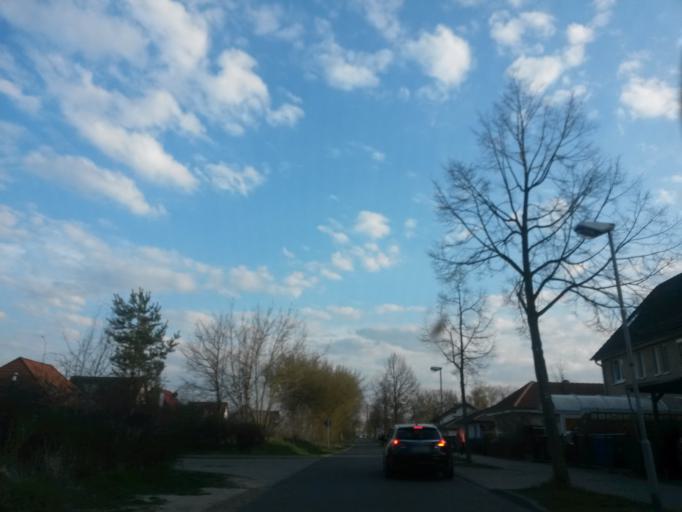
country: DE
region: Brandenburg
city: Strausberg
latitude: 52.5945
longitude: 13.9081
